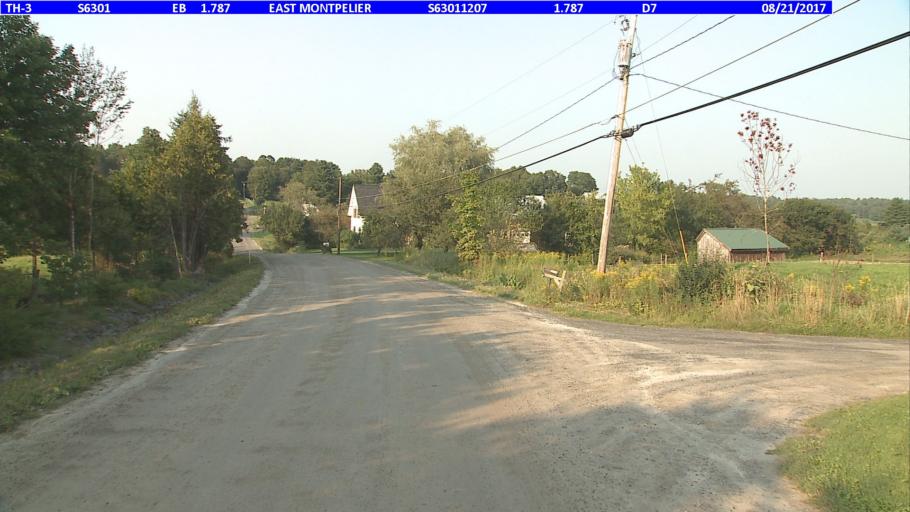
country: US
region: Vermont
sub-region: Washington County
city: Montpelier
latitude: 44.2846
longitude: -72.5227
